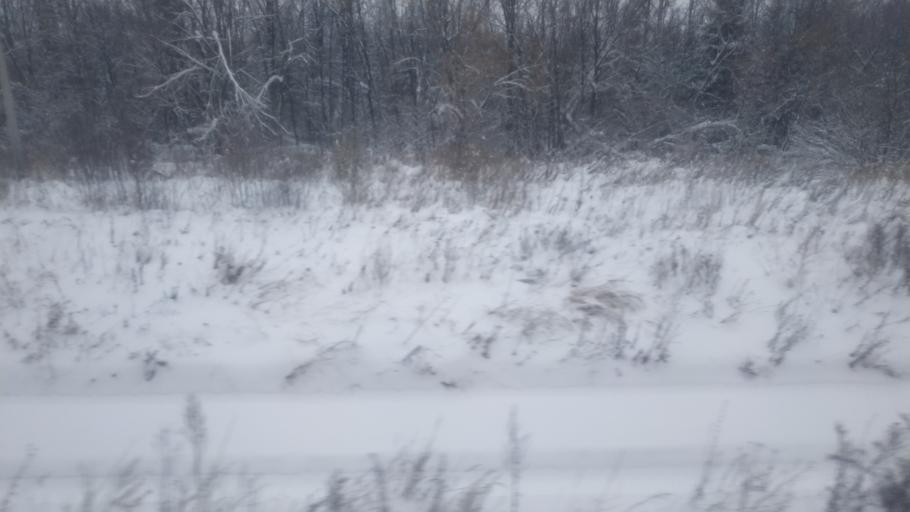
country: RU
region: Udmurtiya
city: Kiyasovo
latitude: 56.5013
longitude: 53.3697
